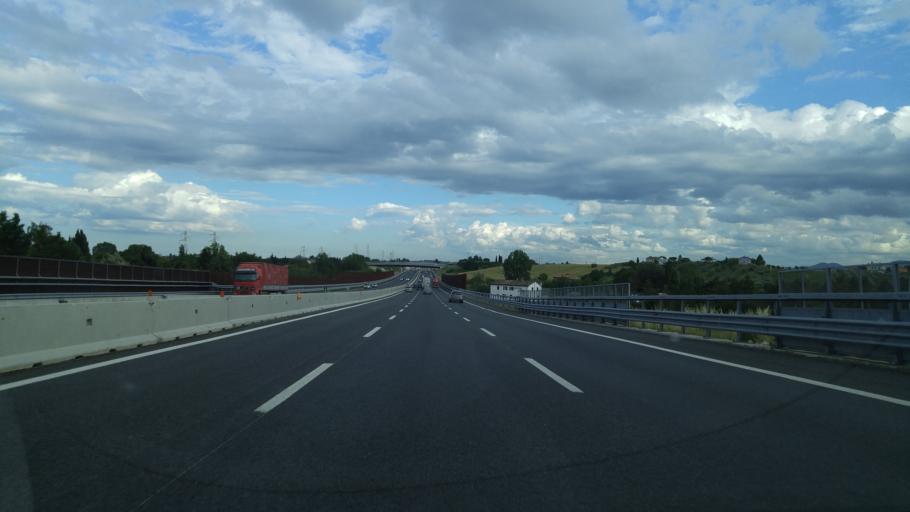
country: IT
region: Emilia-Romagna
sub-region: Provincia di Rimini
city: Rivazzurra
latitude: 44.0152
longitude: 12.5884
